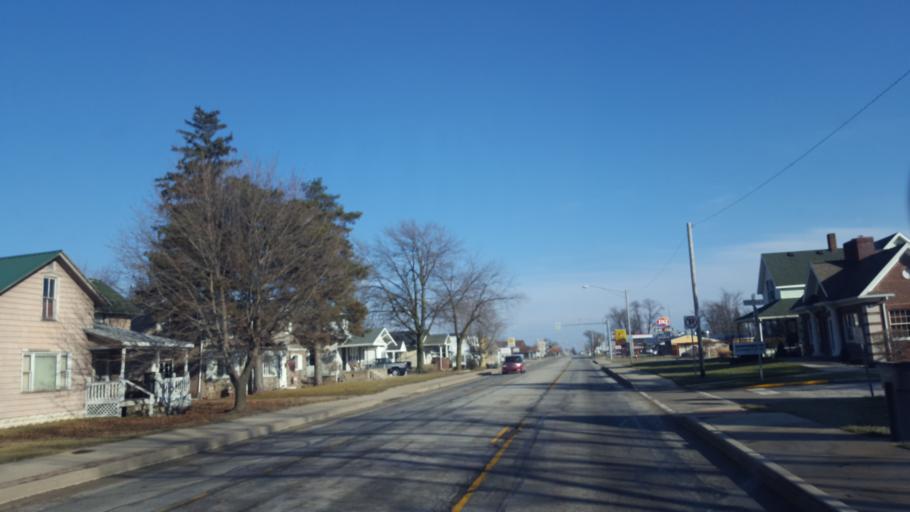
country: US
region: Indiana
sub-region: Elkhart County
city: Nappanee
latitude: 41.4426
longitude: -85.9905
